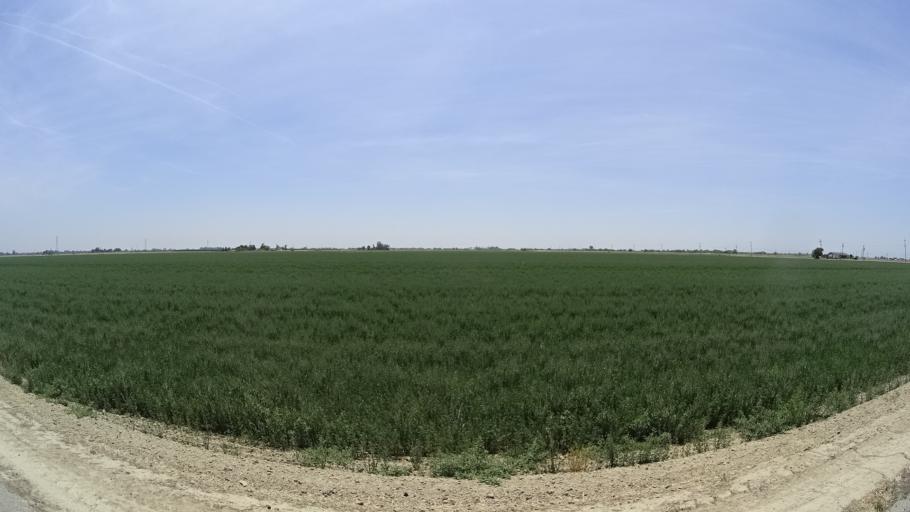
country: US
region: California
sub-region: Fresno County
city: Riverdale
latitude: 36.4054
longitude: -119.9019
